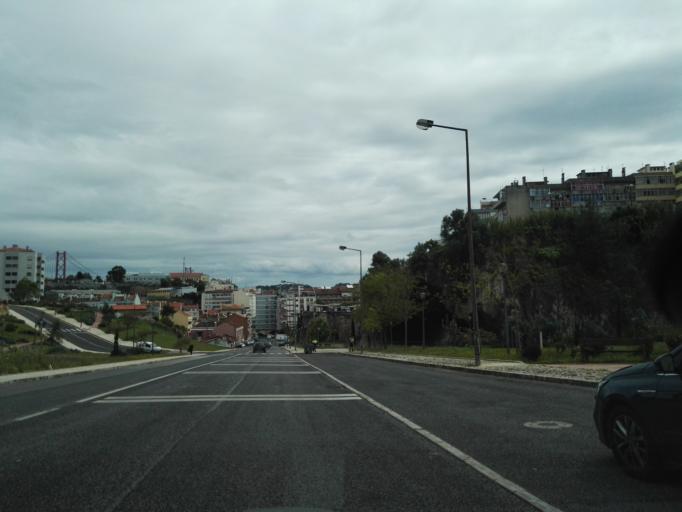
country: PT
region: Lisbon
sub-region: Oeiras
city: Alges
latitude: 38.7067
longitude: -9.1932
